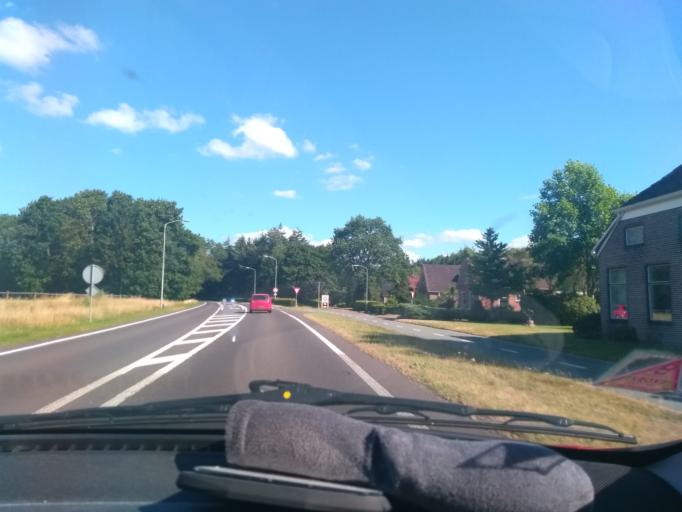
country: NL
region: Drenthe
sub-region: Gemeente Tynaarlo
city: Vries
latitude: 53.0836
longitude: 6.5684
